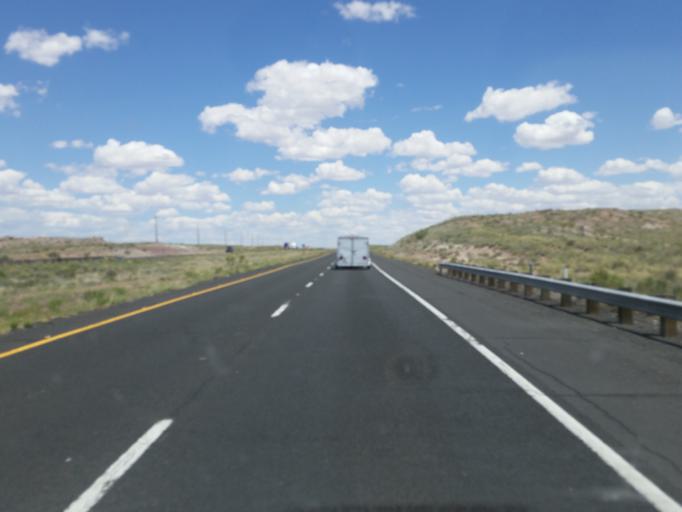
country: US
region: Arizona
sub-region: Navajo County
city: Holbrook
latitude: 34.9909
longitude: -109.9827
